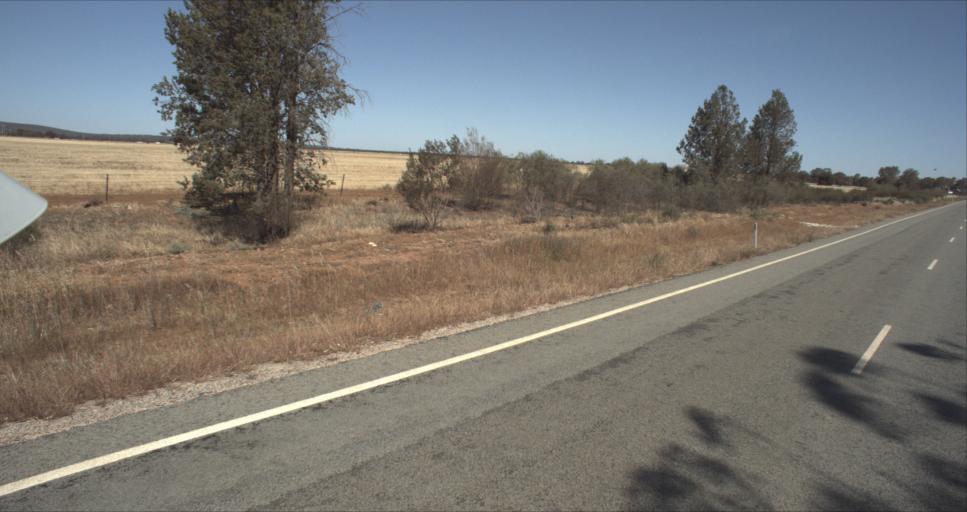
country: AU
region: New South Wales
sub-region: Leeton
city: Leeton
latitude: -34.4894
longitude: 146.4327
